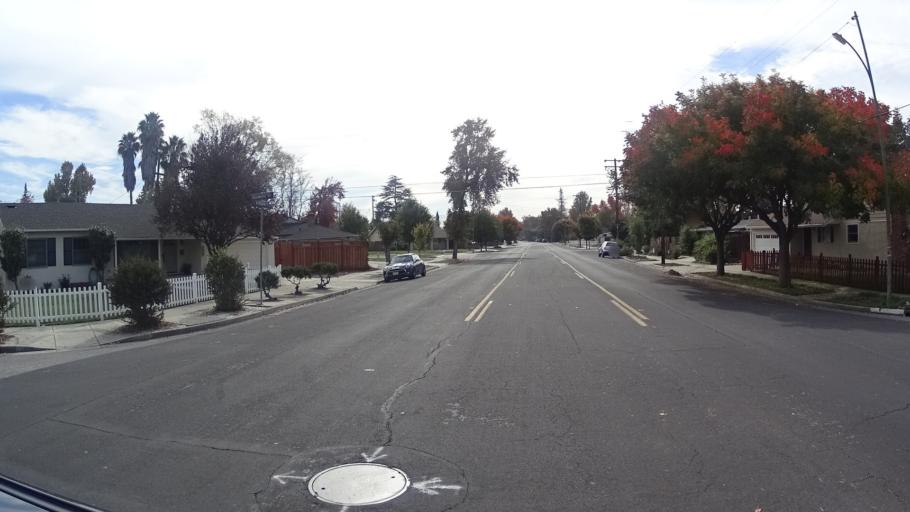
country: US
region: California
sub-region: Santa Clara County
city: Burbank
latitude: 37.3370
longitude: -121.9435
